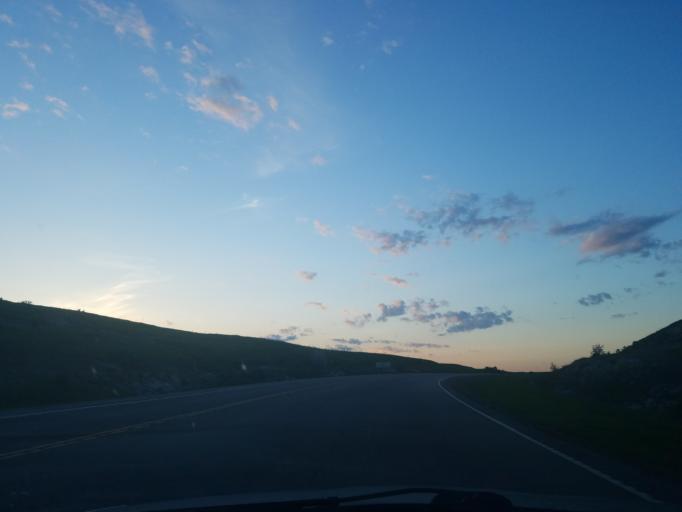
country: US
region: North Dakota
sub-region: McKenzie County
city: Watford City
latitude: 47.6142
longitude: -103.2689
